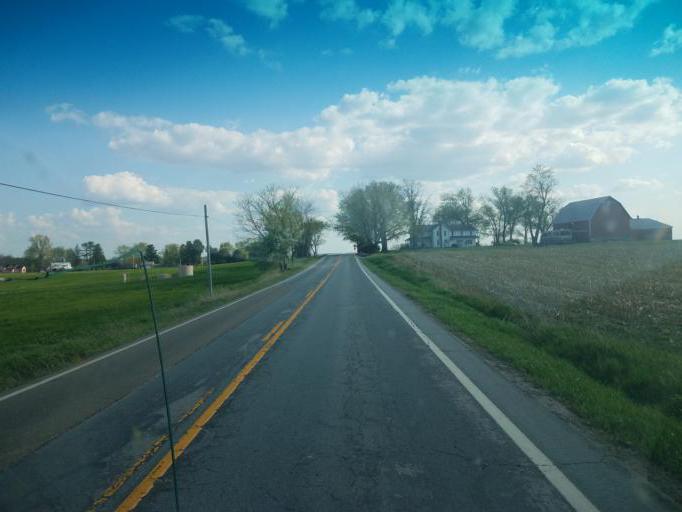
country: US
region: Ohio
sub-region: Wayne County
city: Shreve
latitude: 40.7006
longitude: -81.9505
